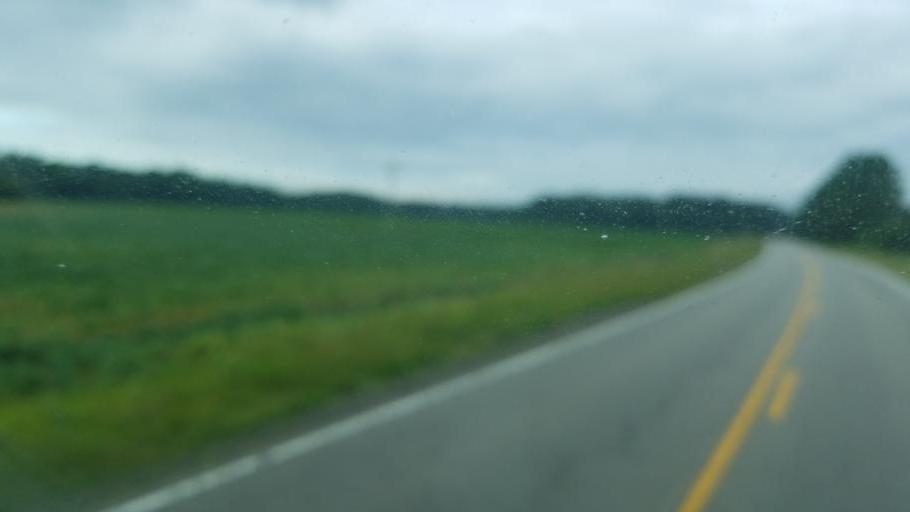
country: US
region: North Carolina
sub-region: Tyrrell County
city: Columbia
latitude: 35.9301
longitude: -76.1848
